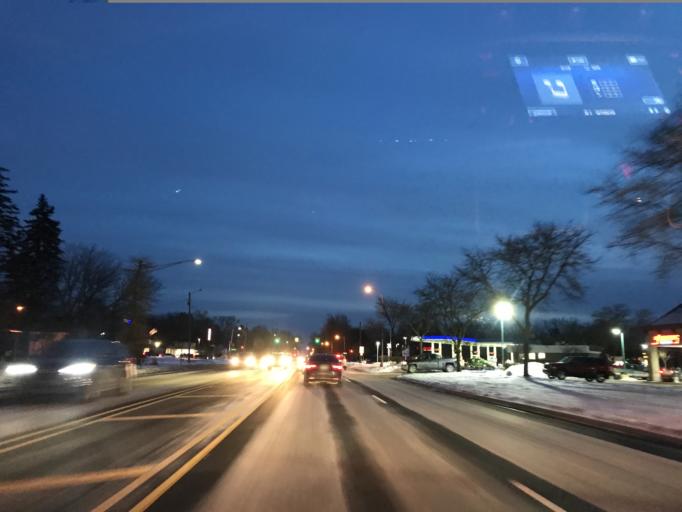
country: US
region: Michigan
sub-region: Wayne County
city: Redford
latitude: 42.4147
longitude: -83.3157
